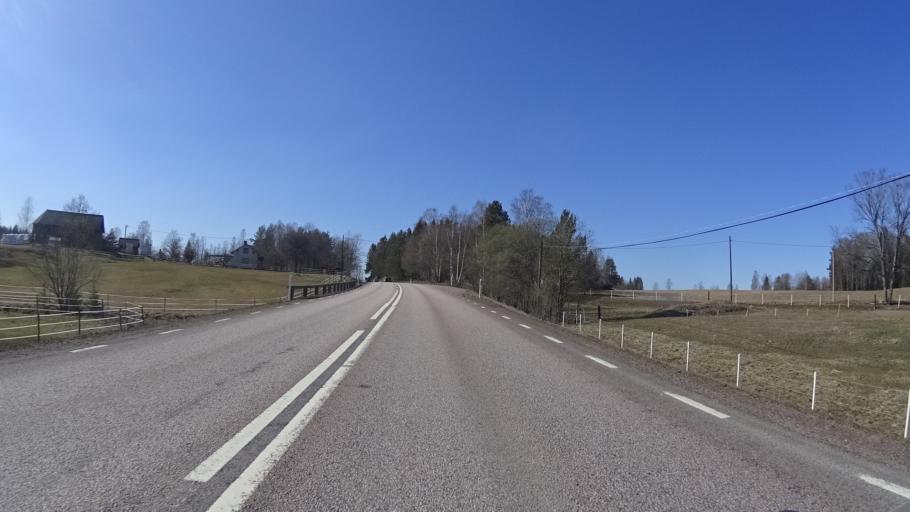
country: SE
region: Vaermland
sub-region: Karlstads Kommun
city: Edsvalla
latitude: 59.5386
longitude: 13.1004
